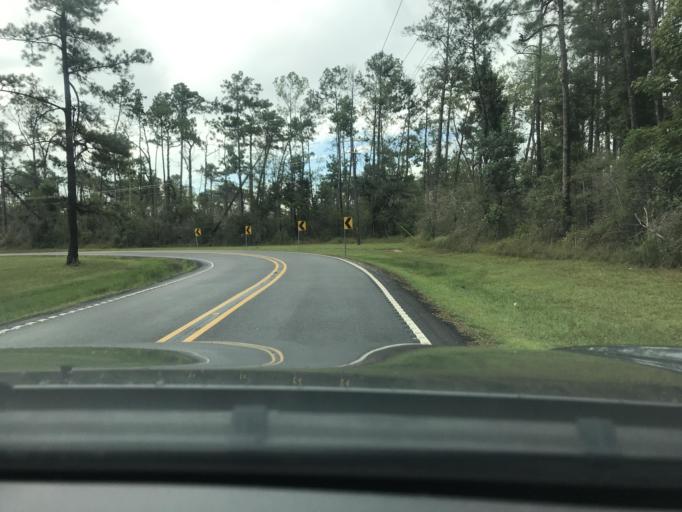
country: US
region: Louisiana
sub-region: Calcasieu Parish
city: Westlake
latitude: 30.3022
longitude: -93.2585
